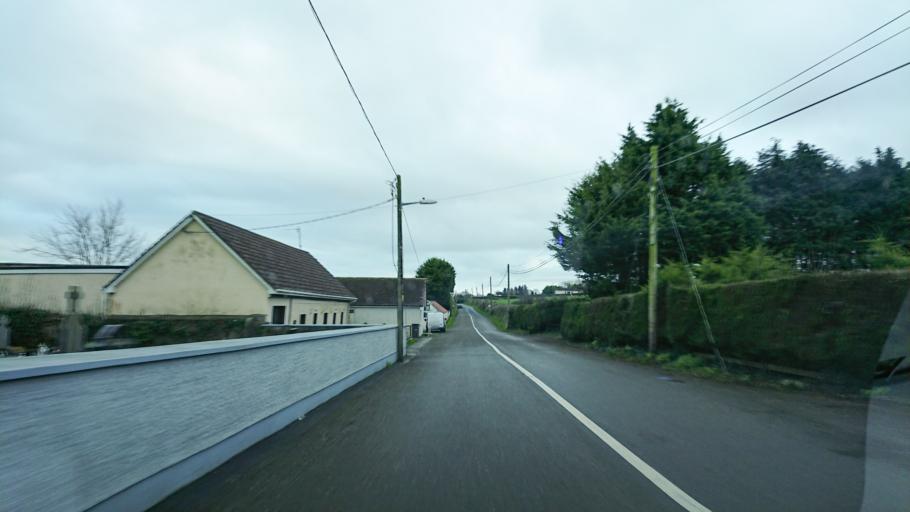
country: IE
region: Munster
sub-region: Waterford
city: Portlaw
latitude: 52.1729
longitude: -7.3987
